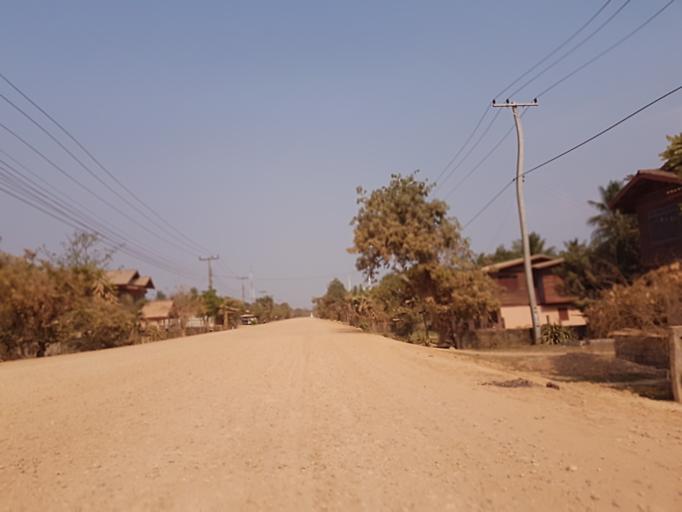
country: TH
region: Nong Khai
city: Nong Khai
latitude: 17.9412
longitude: 102.7951
